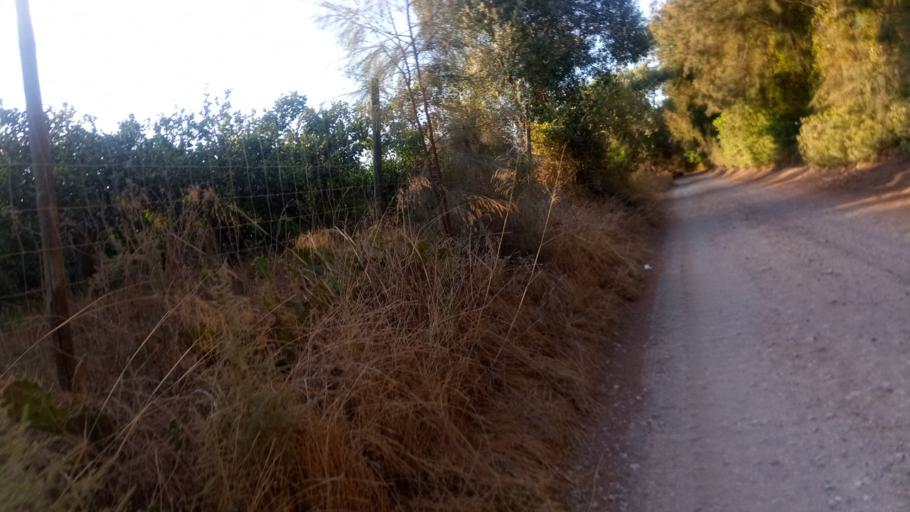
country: PT
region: Faro
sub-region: Tavira
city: Tavira
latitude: 37.1544
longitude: -7.5752
